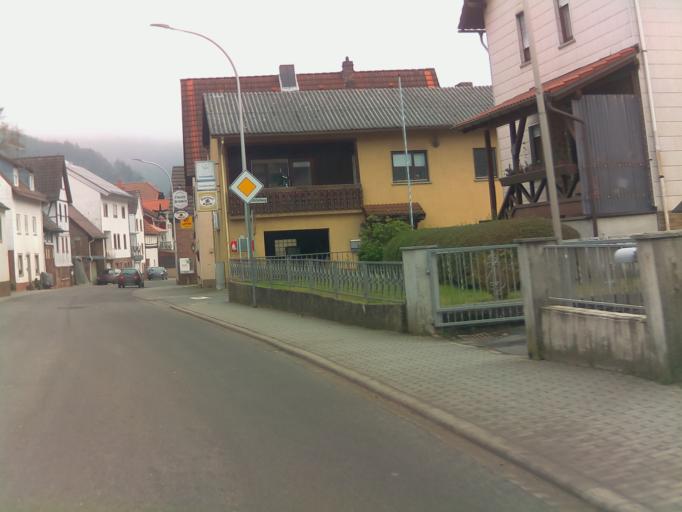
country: DE
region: Bavaria
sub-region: Regierungsbezirk Unterfranken
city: Altenbuch
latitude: 49.8237
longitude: 9.4092
